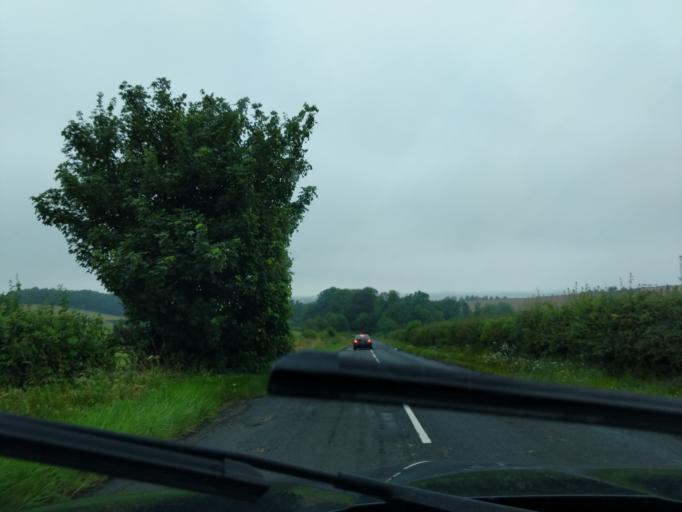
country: GB
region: England
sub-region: Northumberland
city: Lowick
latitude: 55.6593
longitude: -1.9260
